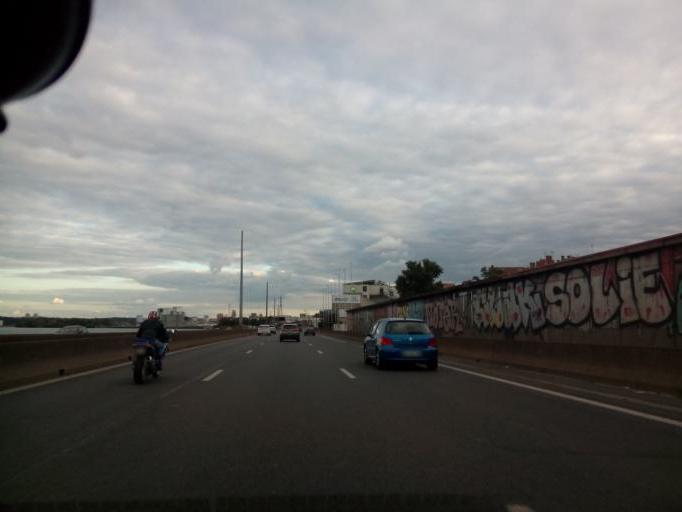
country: FR
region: Rhone-Alpes
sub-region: Departement du Rhone
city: La Mulatiere
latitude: 45.7184
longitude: 4.8186
